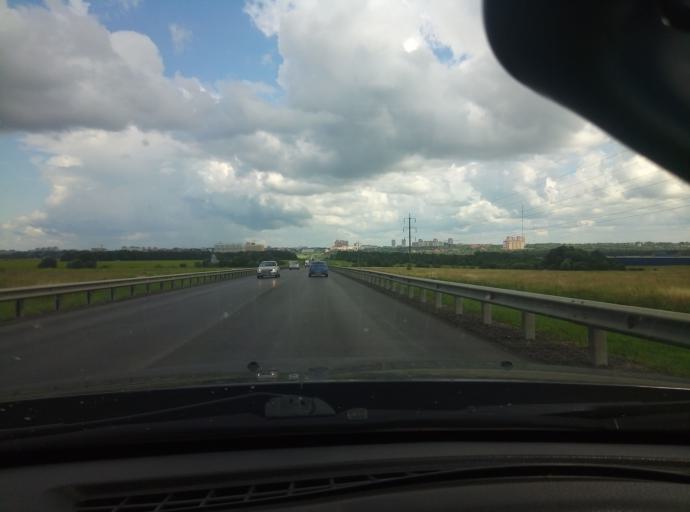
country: RU
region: Tula
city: Kosaya Gora
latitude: 54.1574
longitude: 37.5212
